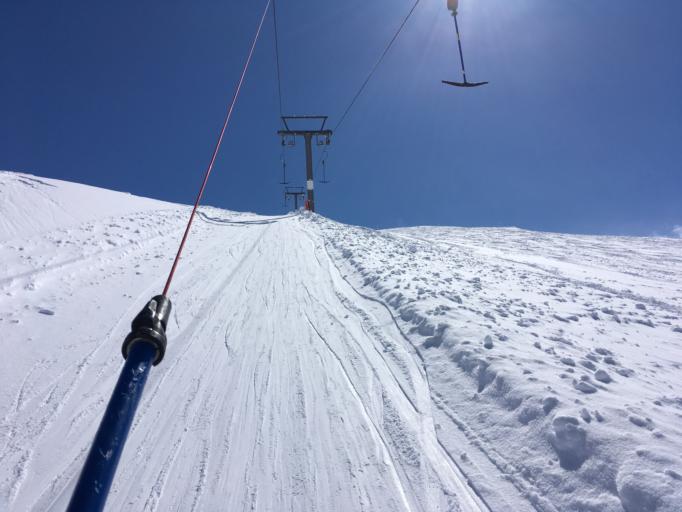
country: CH
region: Grisons
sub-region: Maloja District
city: Promontogno
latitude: 46.4417
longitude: 9.6368
